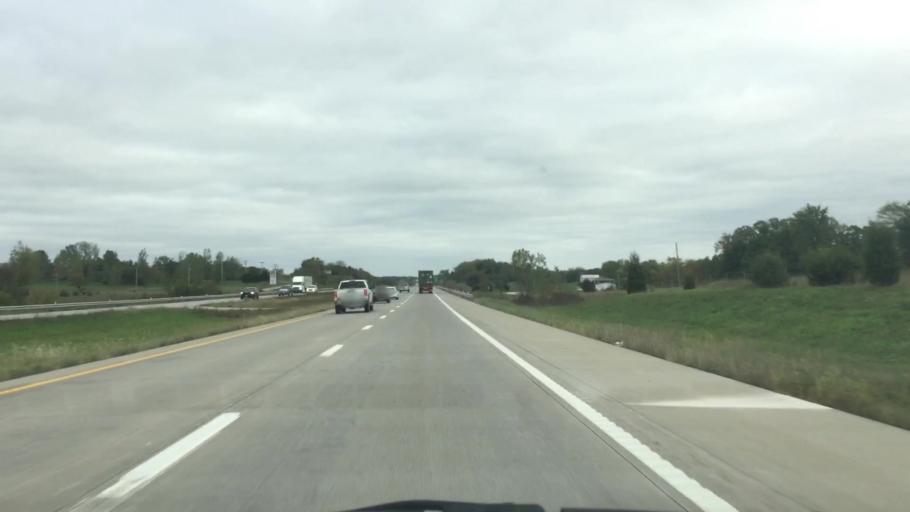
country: US
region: Missouri
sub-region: Clinton County
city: Cameron
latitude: 39.6564
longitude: -94.2384
